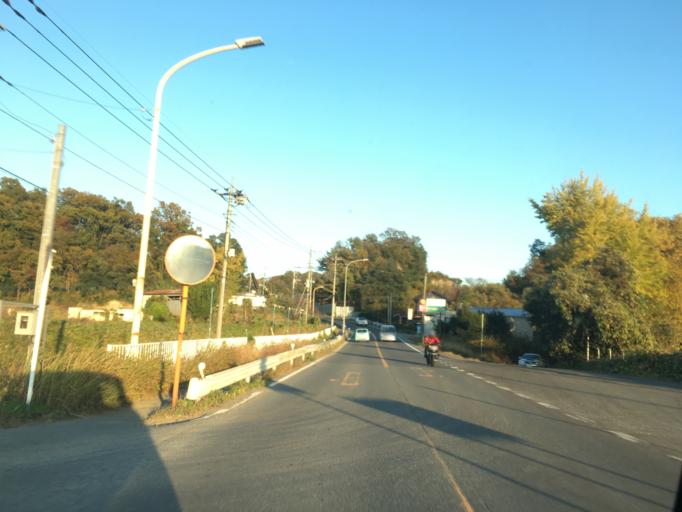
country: JP
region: Saitama
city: Fukiage-fujimi
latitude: 36.0467
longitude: 139.4202
